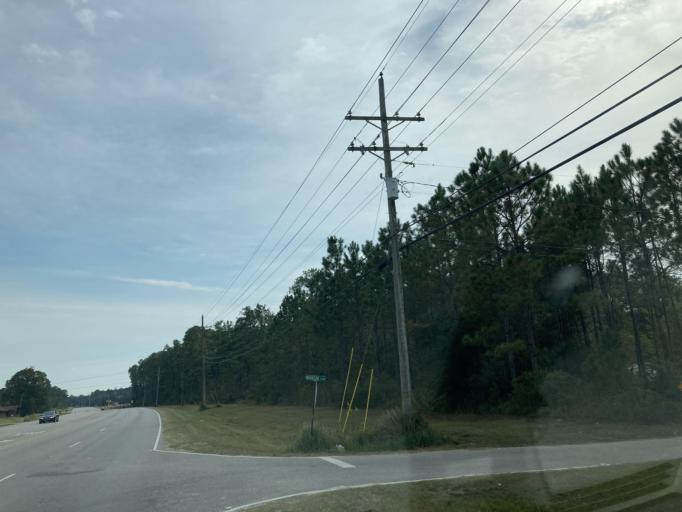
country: US
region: Mississippi
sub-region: Jackson County
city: Saint Martin
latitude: 30.4741
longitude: -88.8495
